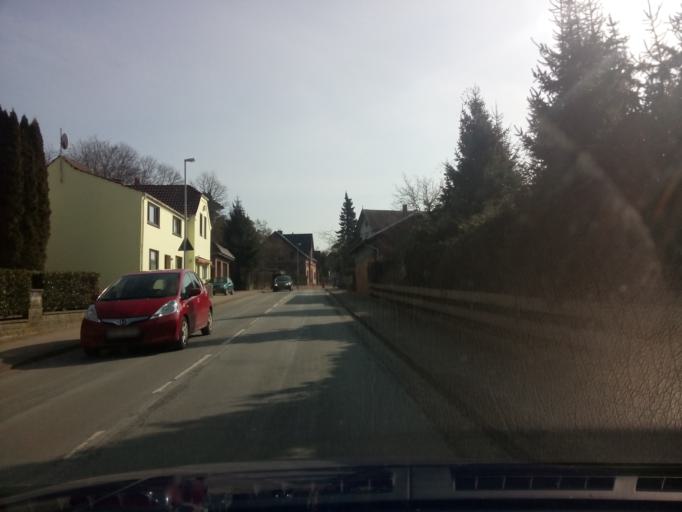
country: DE
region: Lower Saxony
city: Ritterhude
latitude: 53.1786
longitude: 8.7453
